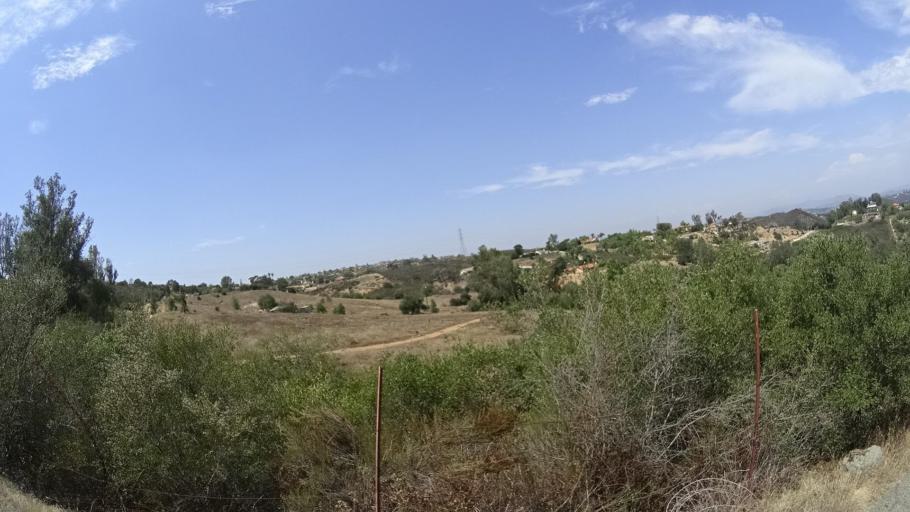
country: US
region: California
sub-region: San Diego County
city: Hidden Meadows
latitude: 33.2191
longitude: -117.0900
